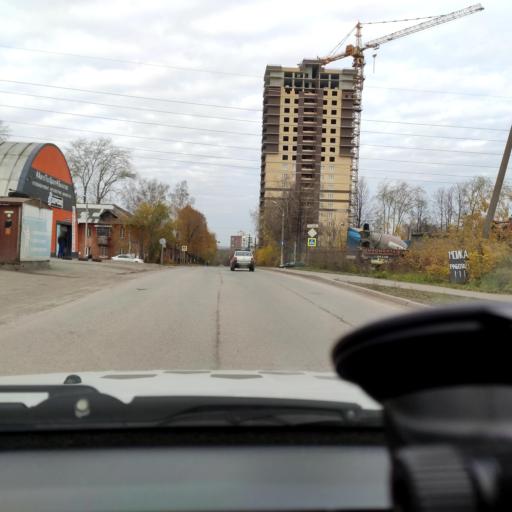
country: RU
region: Perm
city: Kondratovo
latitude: 57.9727
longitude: 56.1810
